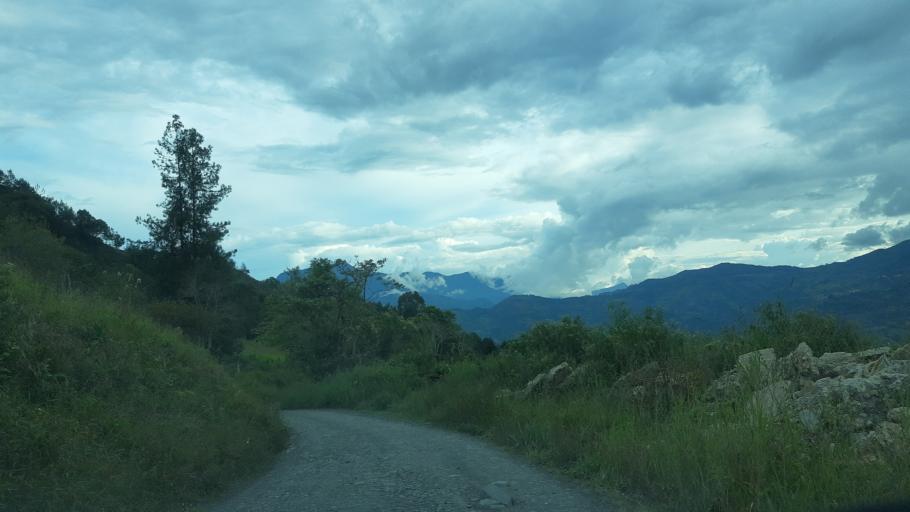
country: CO
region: Boyaca
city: Garagoa
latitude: 4.9844
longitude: -73.3230
